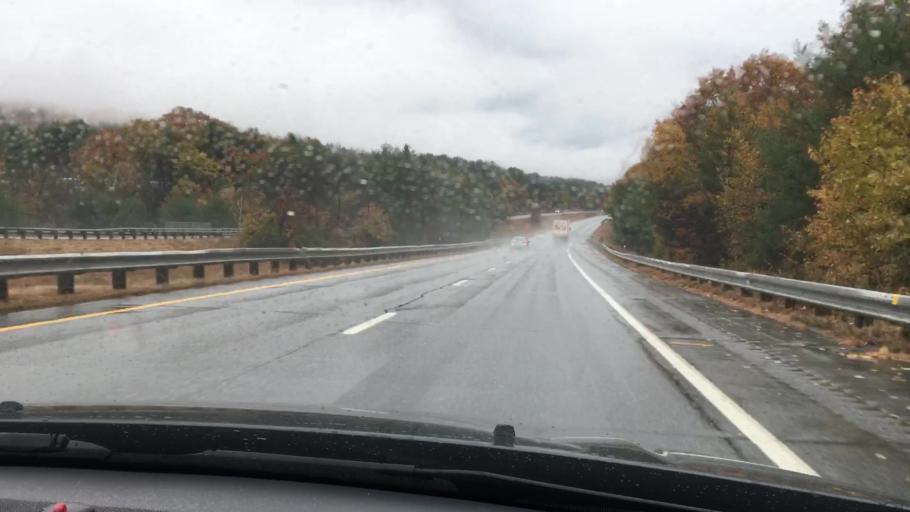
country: US
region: New Hampshire
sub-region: Grafton County
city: Ashland
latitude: 43.6875
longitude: -71.6427
